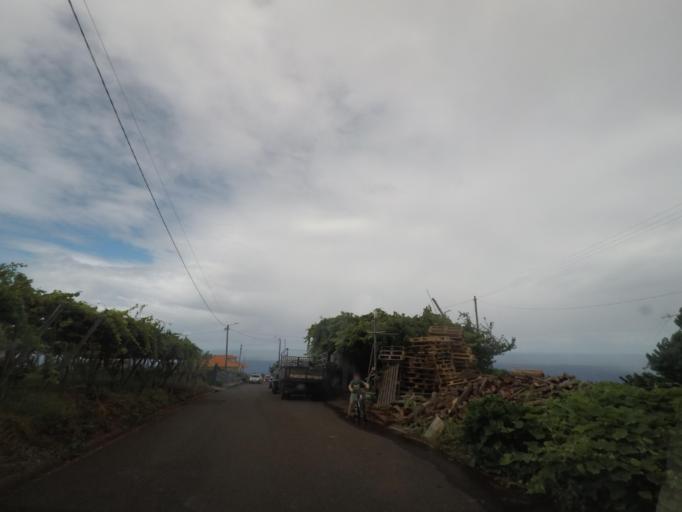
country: PT
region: Madeira
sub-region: Santana
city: Santana
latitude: 32.8333
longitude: -16.9121
